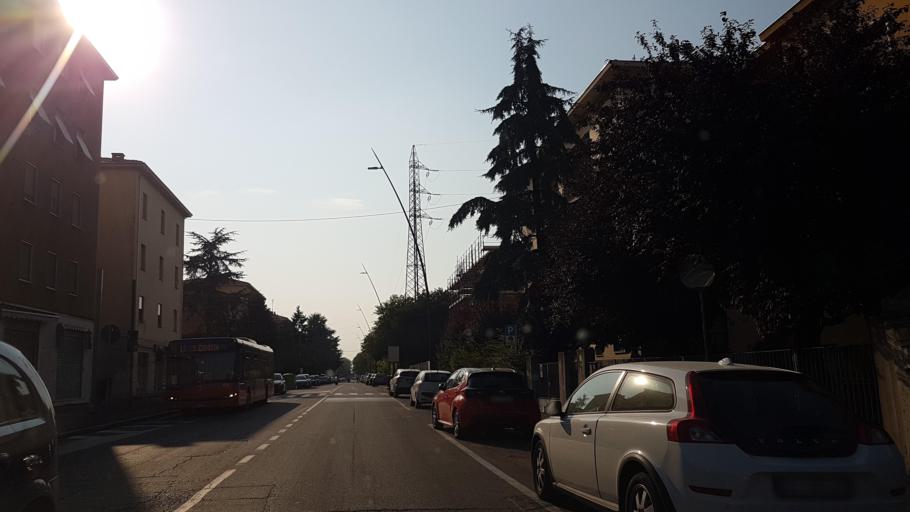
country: IT
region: Emilia-Romagna
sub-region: Provincia di Parma
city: Parma
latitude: 44.7967
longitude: 10.3113
